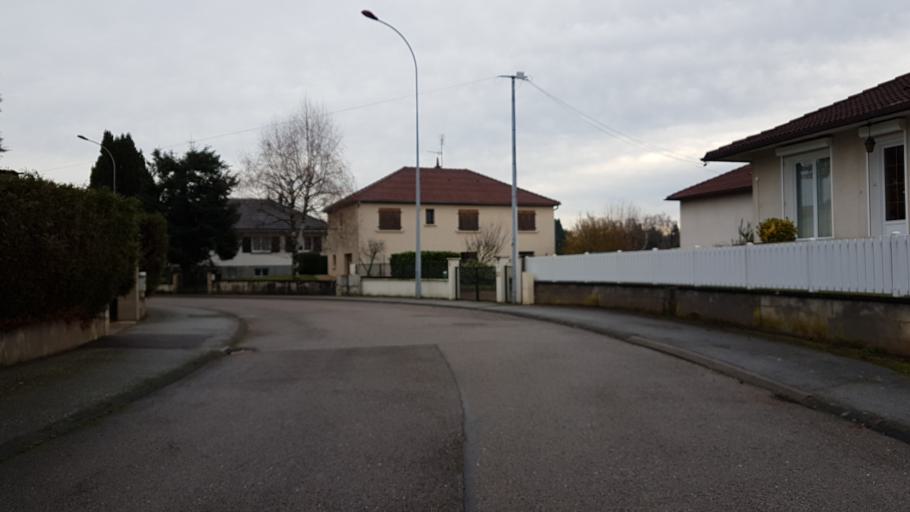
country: FR
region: Franche-Comte
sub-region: Departement de la Haute-Saone
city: Luxeuil-les-Bains
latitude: 47.8124
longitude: 6.3711
